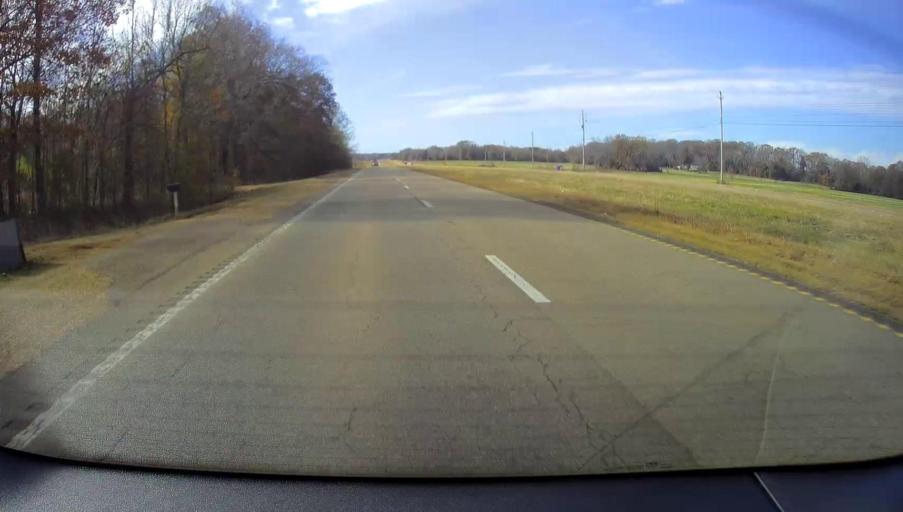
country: US
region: Mississippi
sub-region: Alcorn County
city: Corinth
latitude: 34.9310
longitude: -88.6155
